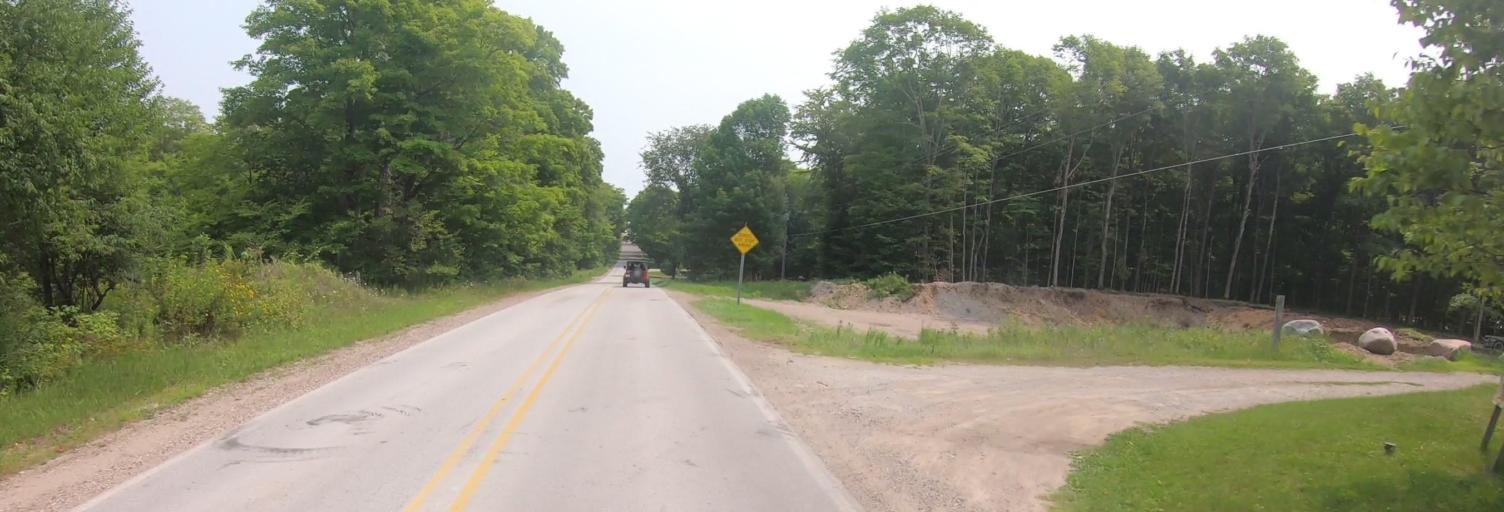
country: CA
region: Ontario
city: Thessalon
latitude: 45.9988
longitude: -83.7295
